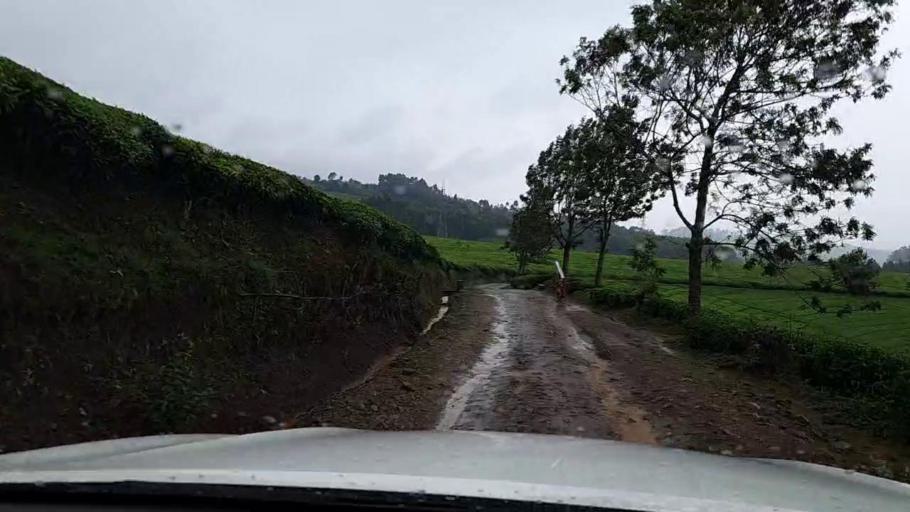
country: RW
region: Western Province
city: Cyangugu
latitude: -2.4559
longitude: 29.0400
